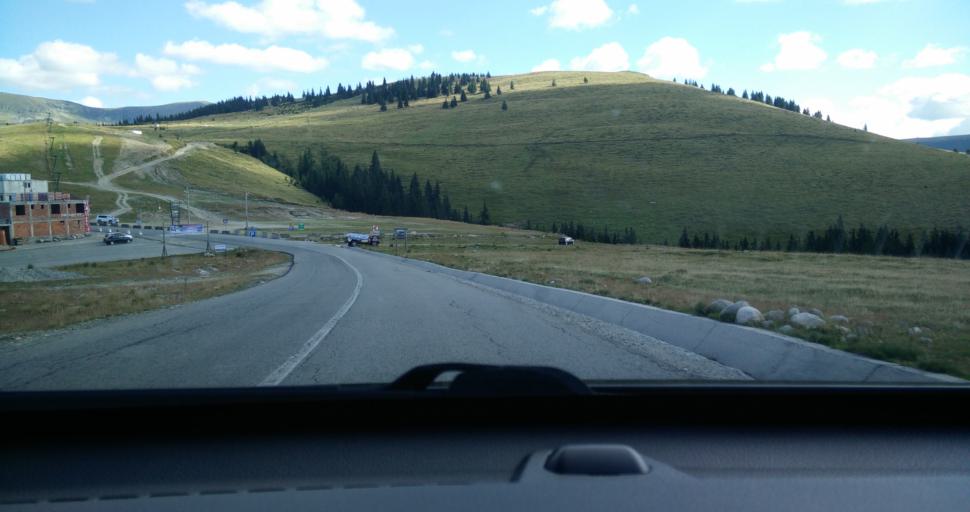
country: RO
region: Gorj
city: Novaci-Straini
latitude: 45.2743
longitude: 23.6897
